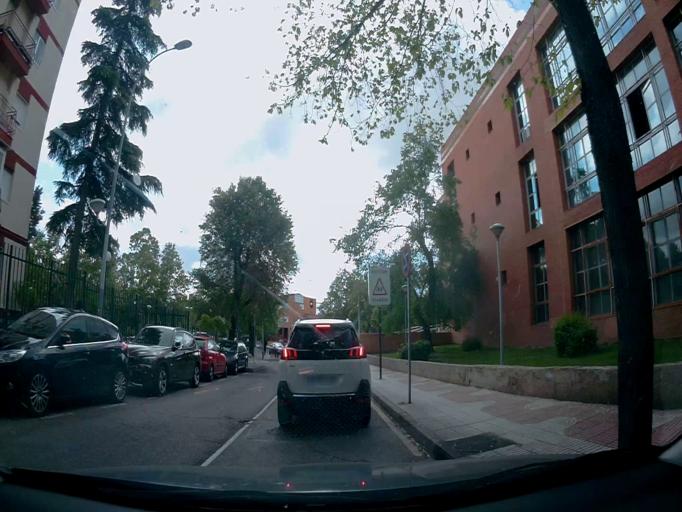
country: ES
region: Madrid
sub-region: Provincia de Madrid
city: Alcorcon
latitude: 40.3448
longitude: -3.8349
